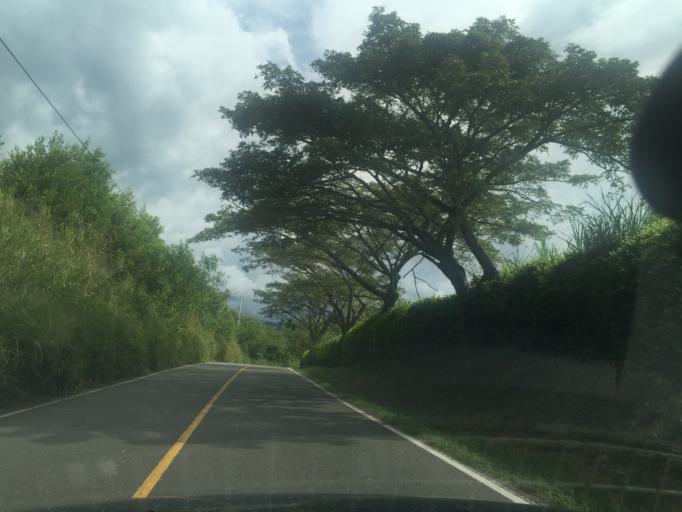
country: CO
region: Valle del Cauca
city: Caicedonia
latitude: 4.3573
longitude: -75.8550
